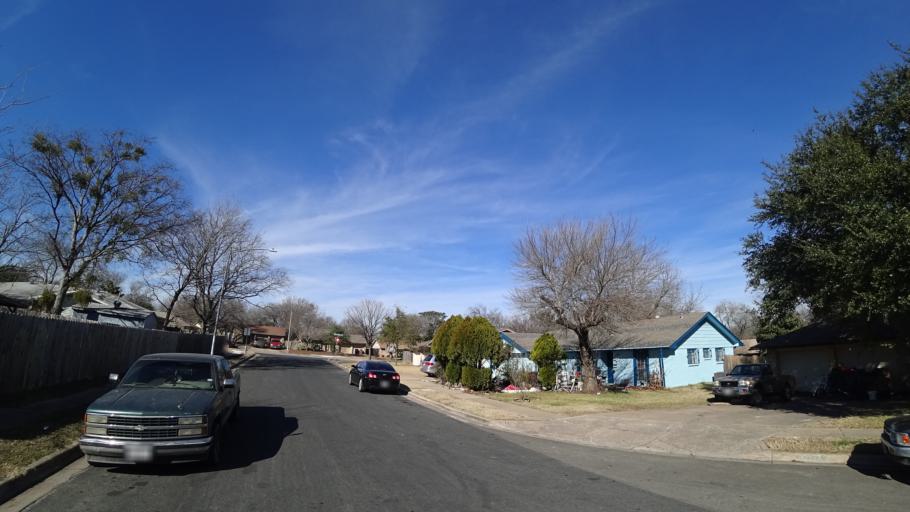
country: US
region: Texas
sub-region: Travis County
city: Wells Branch
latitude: 30.3773
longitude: -97.7081
